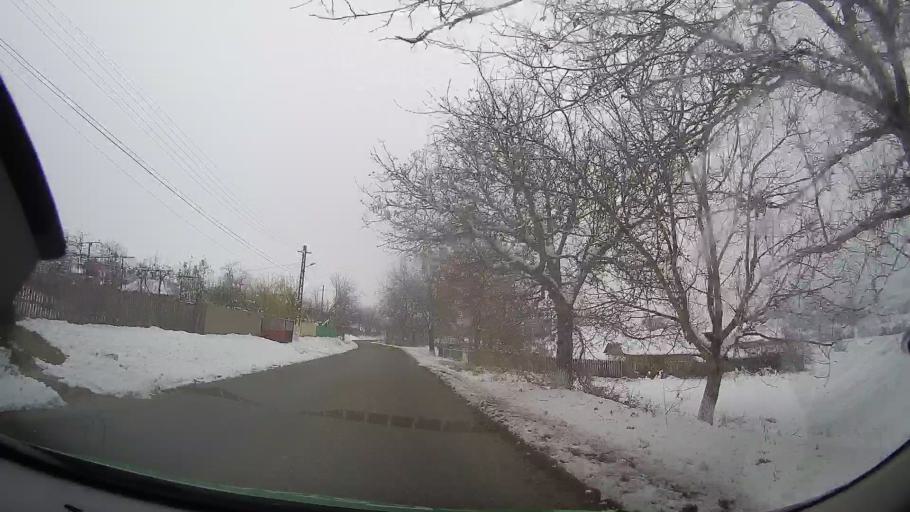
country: RO
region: Bacau
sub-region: Comuna Oncesti
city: Oncesti
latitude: 46.4416
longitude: 27.2665
